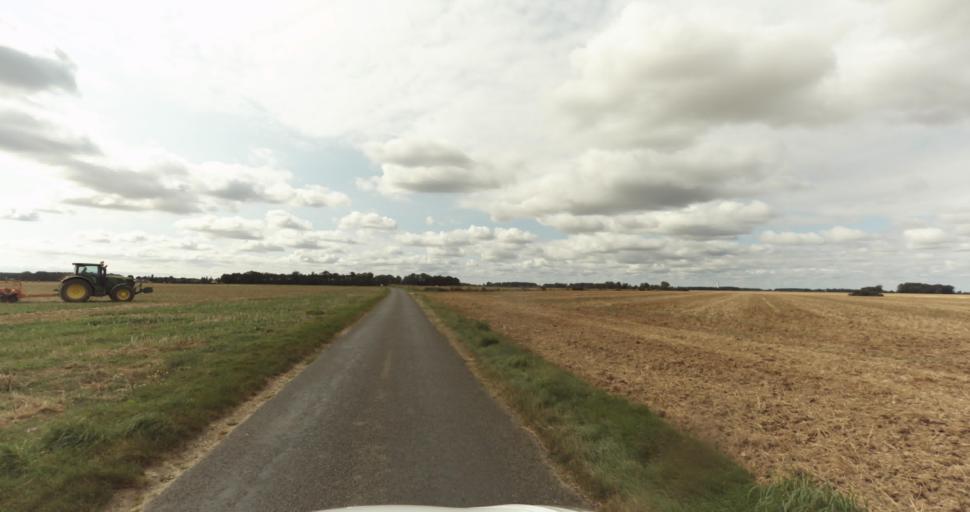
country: FR
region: Haute-Normandie
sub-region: Departement de l'Eure
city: Tillieres-sur-Avre
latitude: 48.7912
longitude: 1.0995
